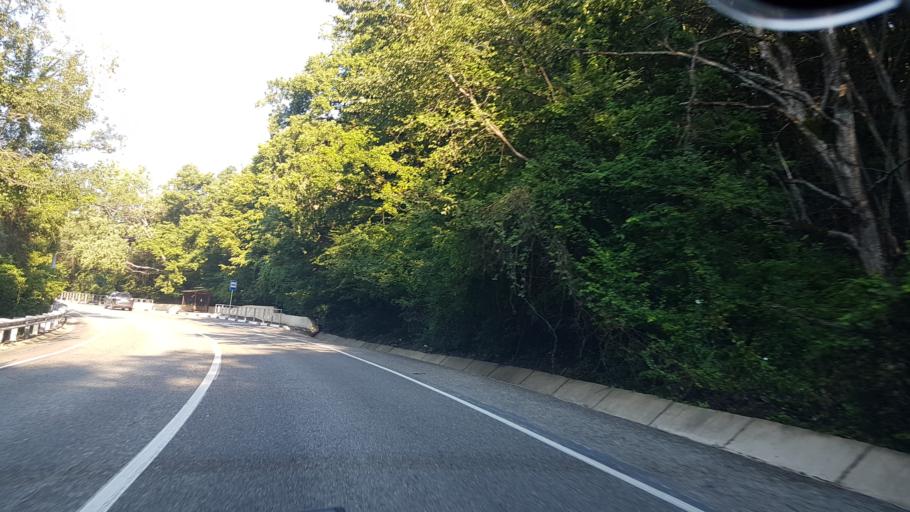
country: RU
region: Krasnodarskiy
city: Vardane
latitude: 43.7537
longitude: 39.5263
